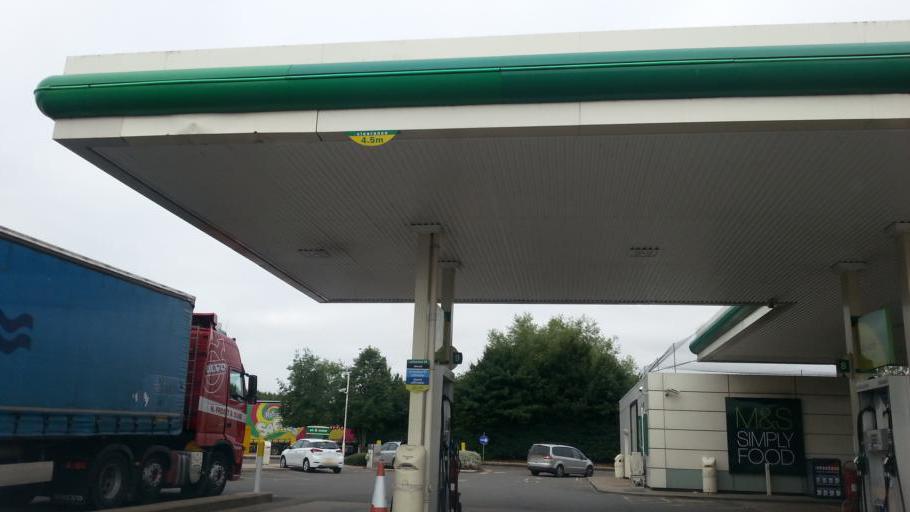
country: GB
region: England
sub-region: Cambridgeshire
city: Brampton
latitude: 52.3313
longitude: -0.2507
